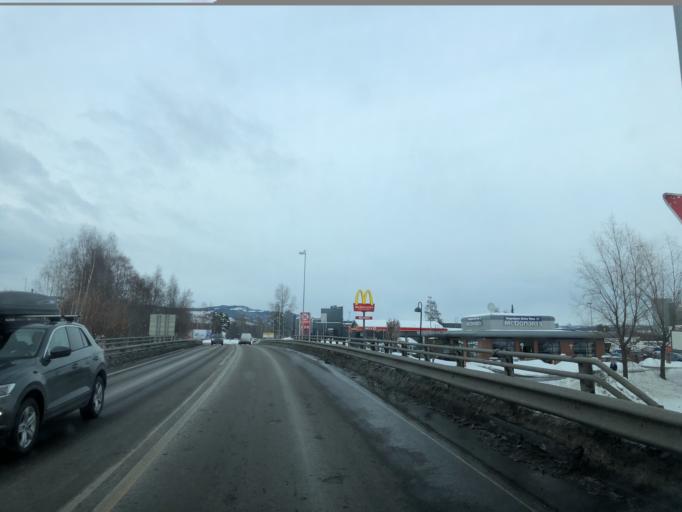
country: NO
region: Oppland
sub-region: Gjovik
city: Gjovik
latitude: 60.7939
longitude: 10.6973
